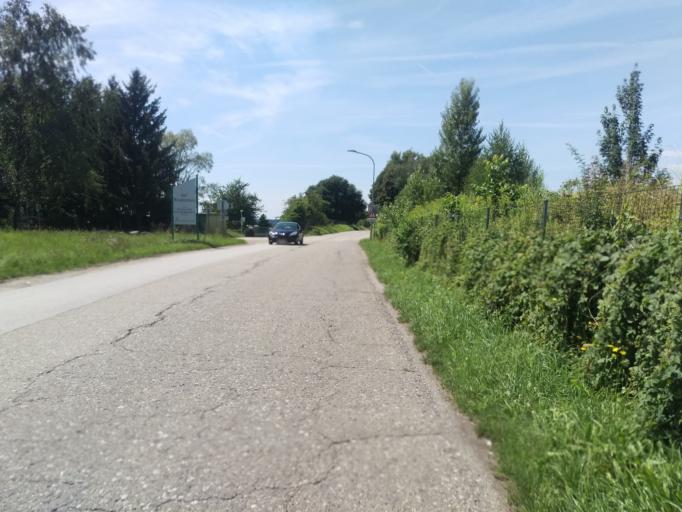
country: AT
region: Styria
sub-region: Politischer Bezirk Graz-Umgebung
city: Seiersberg
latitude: 46.9962
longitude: 15.4249
